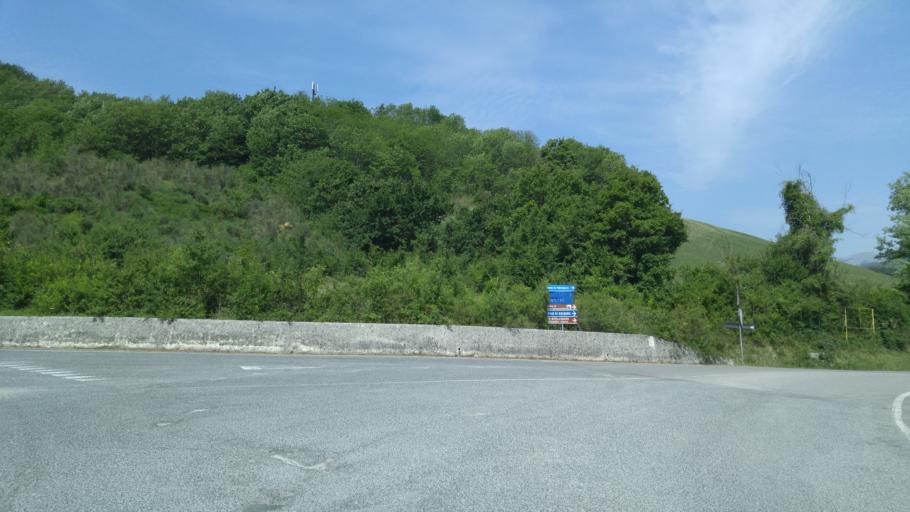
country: IT
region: The Marches
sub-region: Provincia di Pesaro e Urbino
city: Cantiano
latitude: 43.4822
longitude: 12.6204
